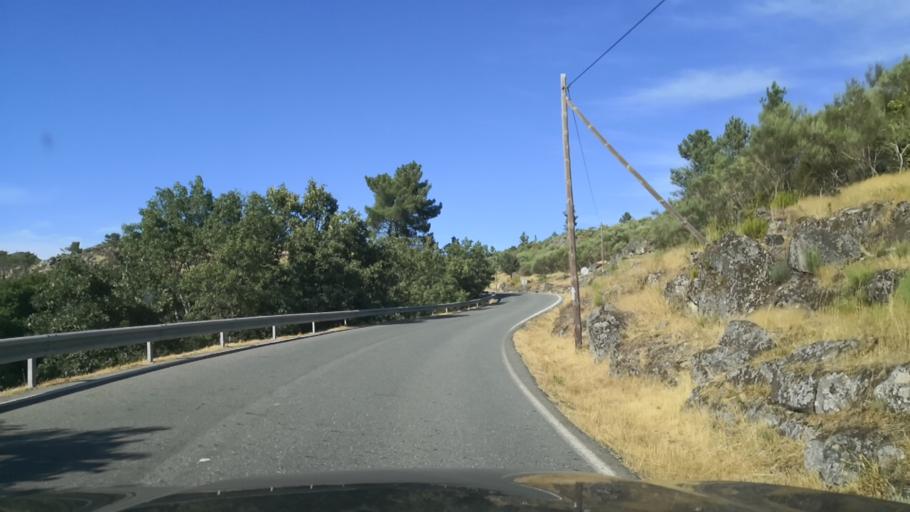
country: PT
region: Vila Real
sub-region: Sabrosa
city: Sabrosa
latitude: 41.3732
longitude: -7.5603
